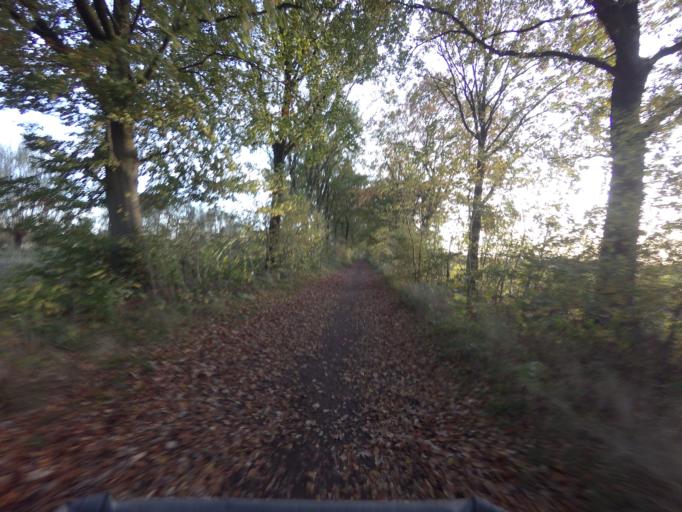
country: NL
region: Utrecht
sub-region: Gemeente De Bilt
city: De Bilt
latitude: 52.1451
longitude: 5.1762
